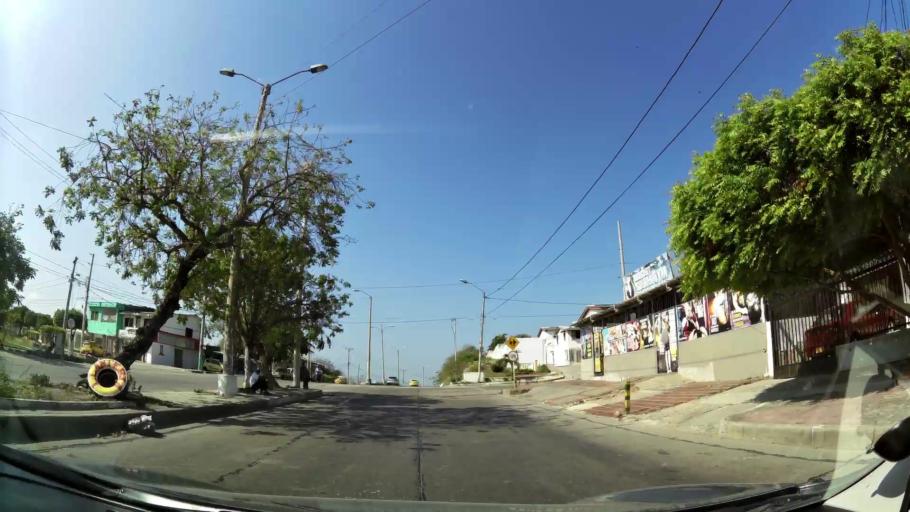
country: CO
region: Atlantico
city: Barranquilla
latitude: 10.9858
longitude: -74.8219
